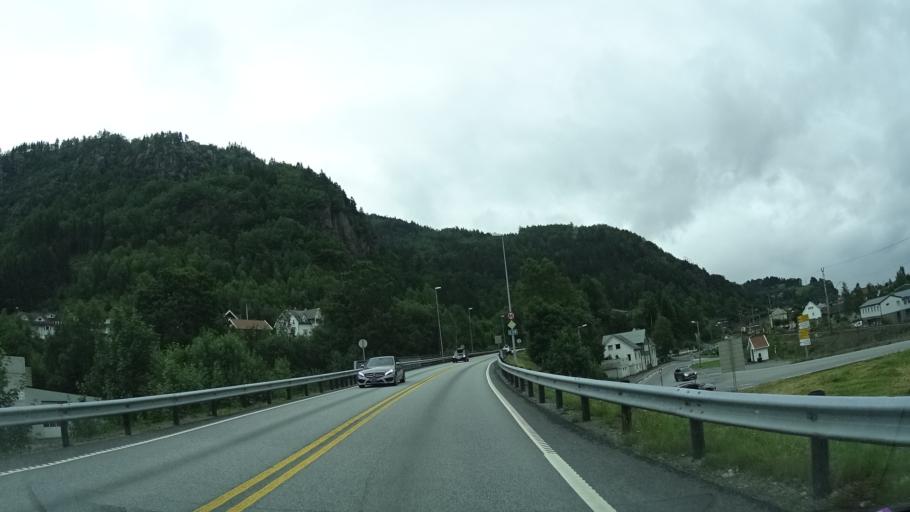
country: NO
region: Rogaland
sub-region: Lund
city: Moi
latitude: 58.4603
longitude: 6.5471
